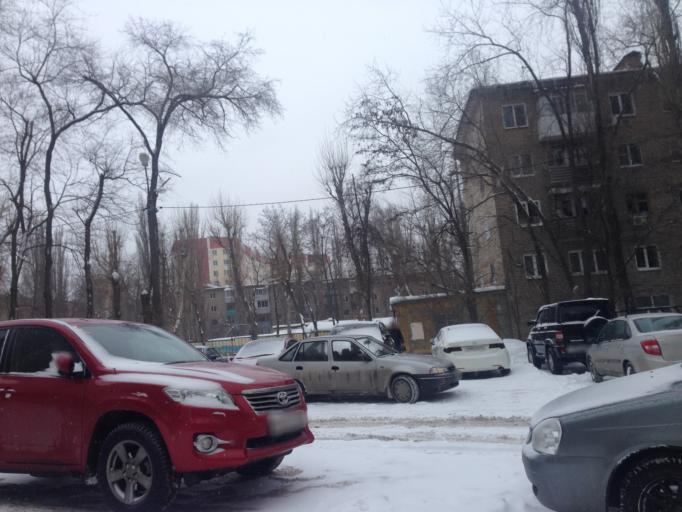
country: RU
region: Voronezj
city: Voronezh
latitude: 51.6581
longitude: 39.1534
